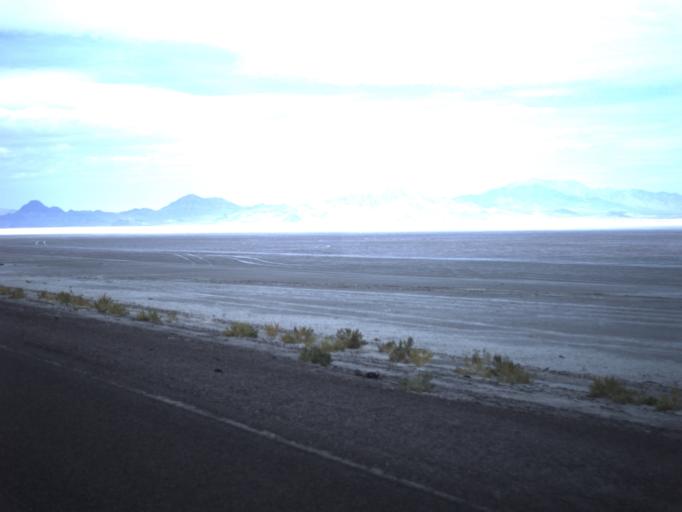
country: US
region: Utah
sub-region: Tooele County
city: Wendover
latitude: 40.7378
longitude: -113.7717
